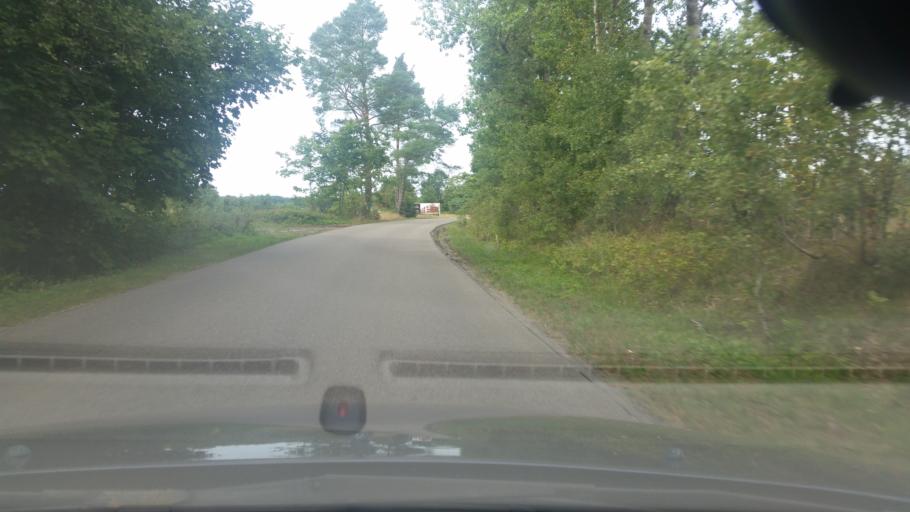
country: PL
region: Pomeranian Voivodeship
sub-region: Powiat leborski
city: Leba
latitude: 54.7278
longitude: 17.6116
